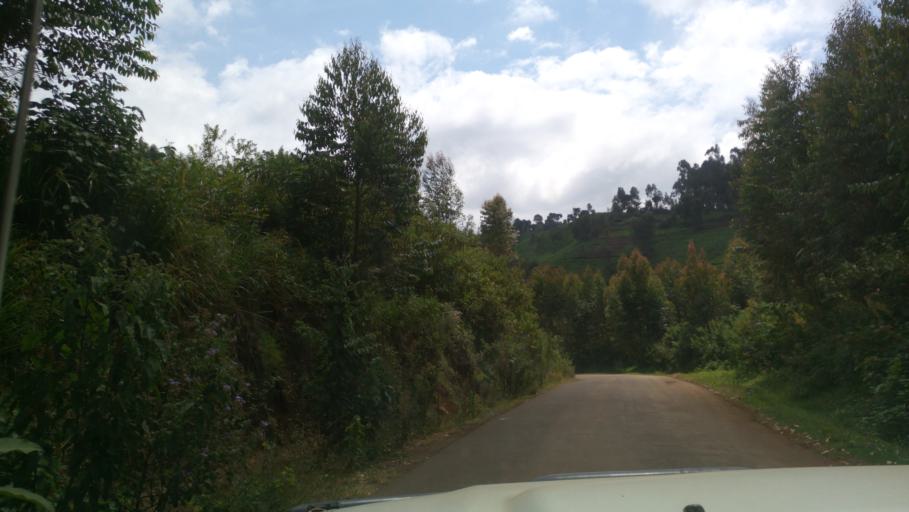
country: KE
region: Murang'a District
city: Kangema
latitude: -0.7689
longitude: 36.8341
